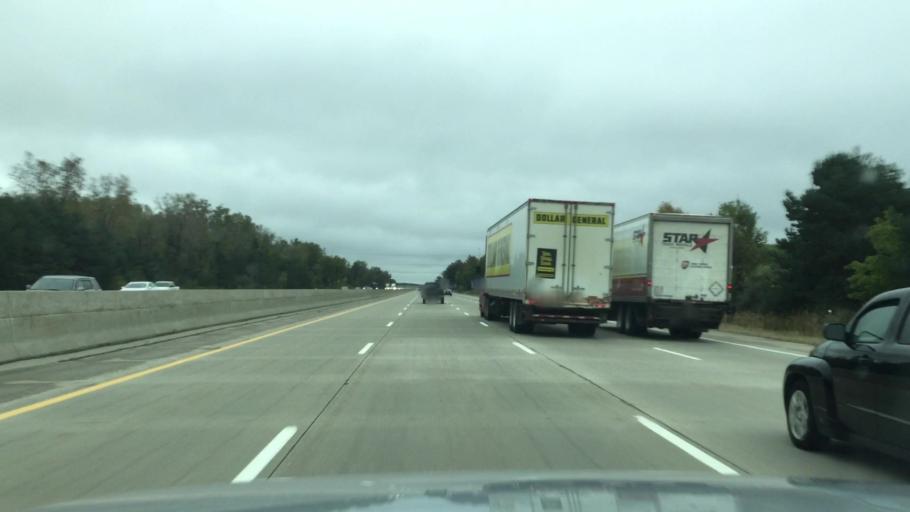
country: US
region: Michigan
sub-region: Genesee County
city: Clio
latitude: 43.2052
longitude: -83.7691
